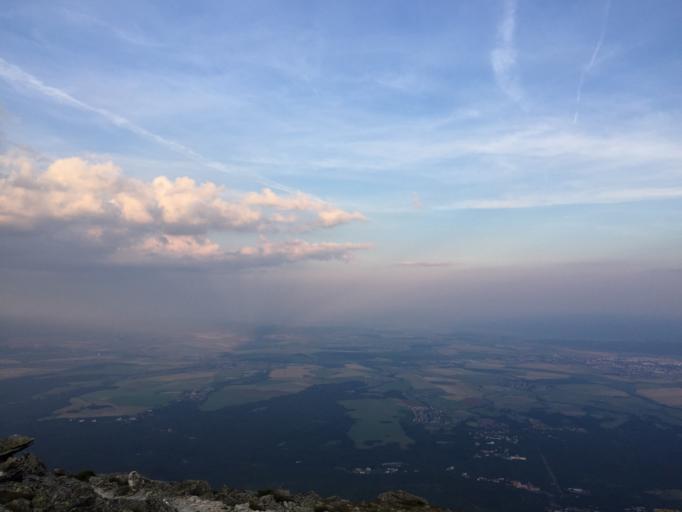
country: SK
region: Presovsky
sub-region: Okres Poprad
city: Vysoke Tatry
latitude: 49.1644
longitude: 20.2003
